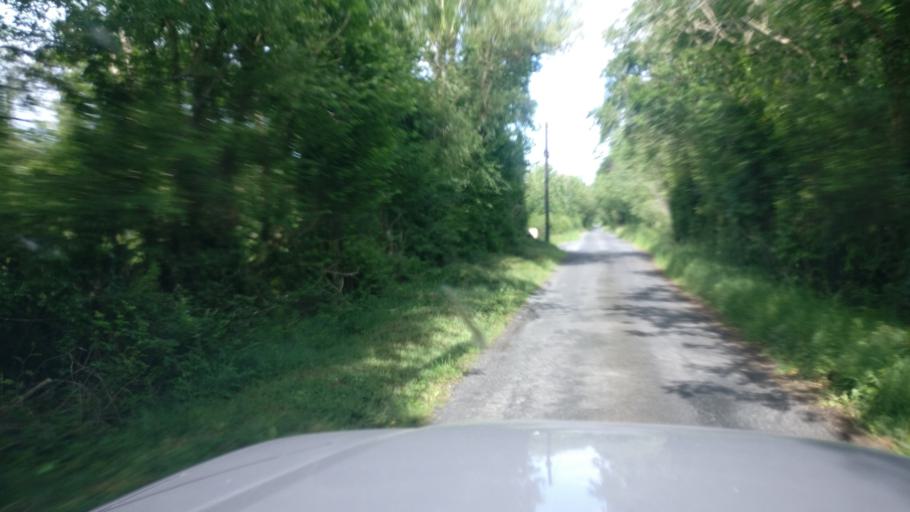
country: IE
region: Connaught
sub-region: County Galway
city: Gort
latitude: 53.0766
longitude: -8.7641
